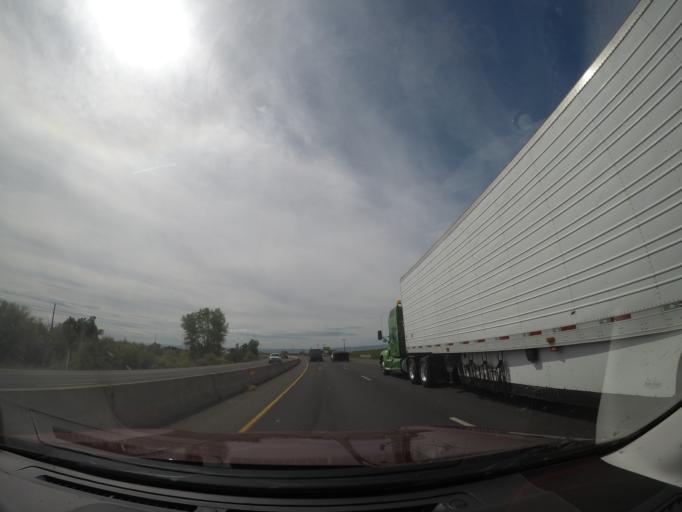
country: US
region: Washington
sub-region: Yakima County
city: Union Gap
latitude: 46.5227
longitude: -120.4804
